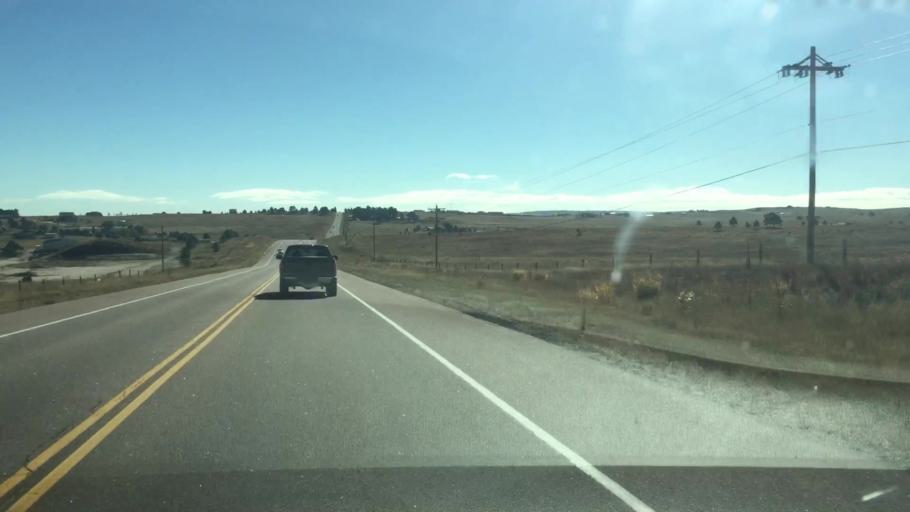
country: US
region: Colorado
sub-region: Elbert County
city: Elizabeth
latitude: 39.3612
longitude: -104.5445
